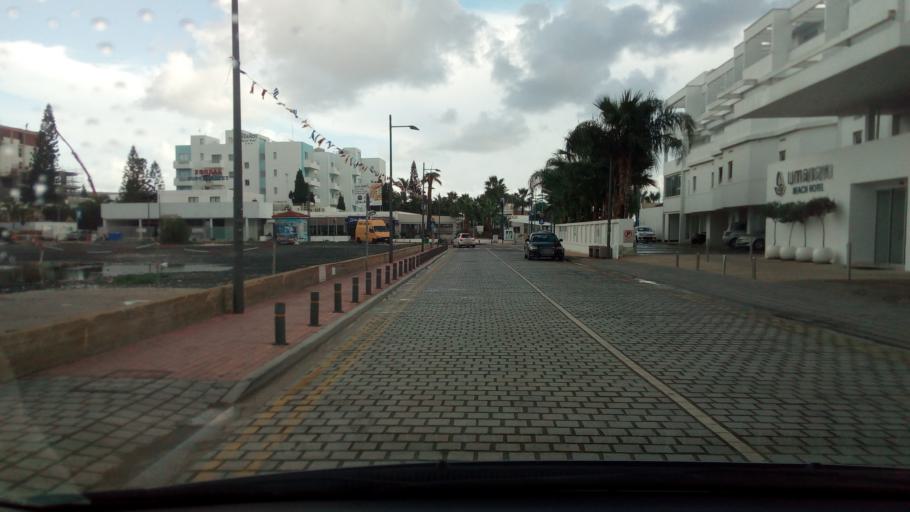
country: CY
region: Ammochostos
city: Ayia Napa
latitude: 34.9833
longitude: 34.0021
